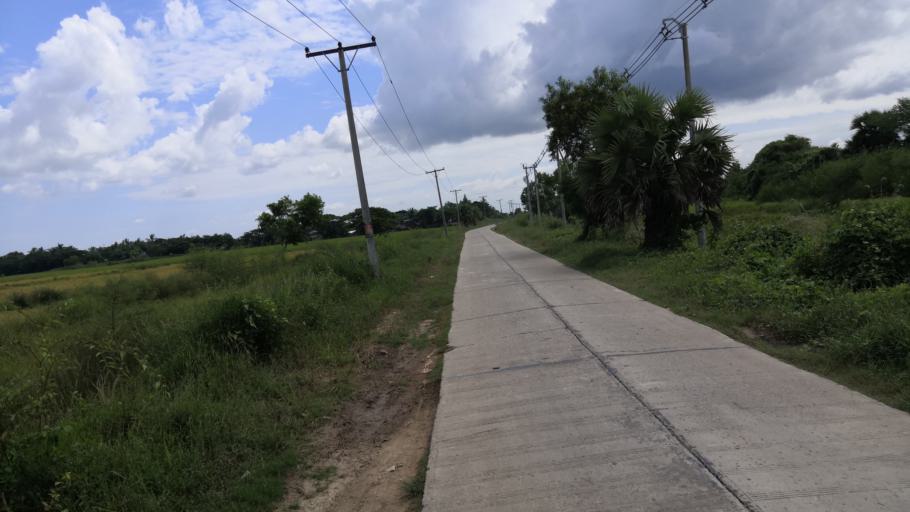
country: MM
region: Yangon
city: Kanbe
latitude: 16.4370
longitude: 96.1587
